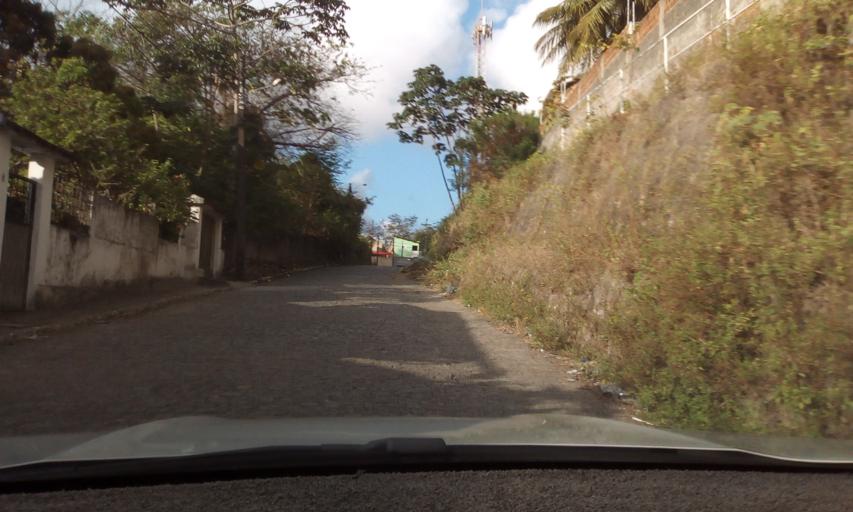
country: BR
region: Paraiba
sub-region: Bayeux
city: Bayeux
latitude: -7.1512
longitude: -34.8950
